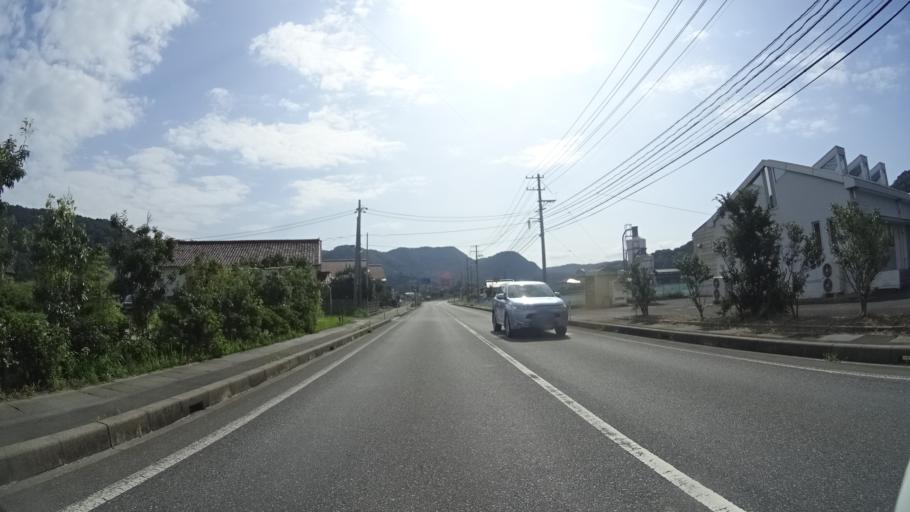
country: JP
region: Shimane
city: Odacho-oda
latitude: 35.1478
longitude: 132.4069
